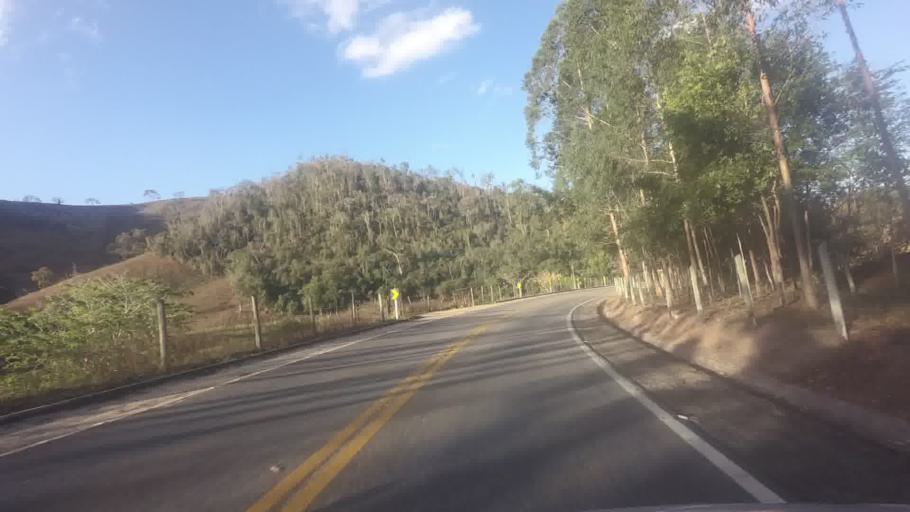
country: BR
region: Espirito Santo
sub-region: Cachoeiro De Itapemirim
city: Cachoeiro de Itapemirim
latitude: -20.8250
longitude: -41.2176
